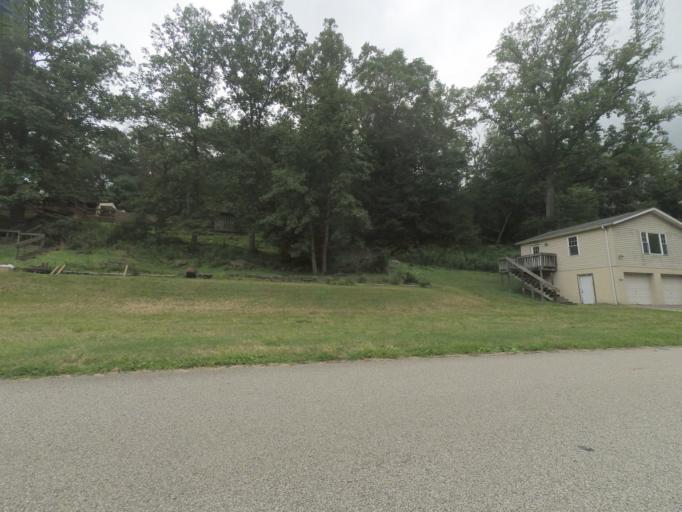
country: US
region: West Virginia
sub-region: Cabell County
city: Huntington
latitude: 38.3876
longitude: -82.4354
